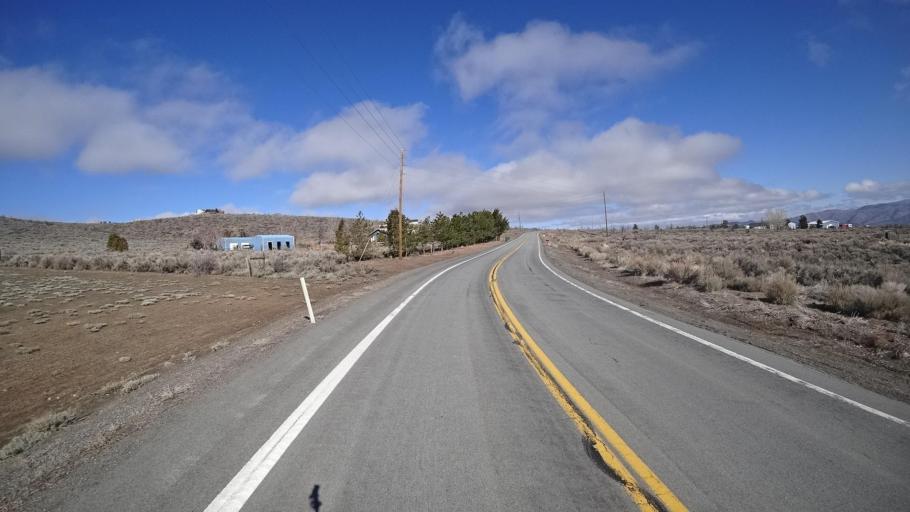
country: US
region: Nevada
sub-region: Washoe County
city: Cold Springs
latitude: 39.7867
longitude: -119.8990
